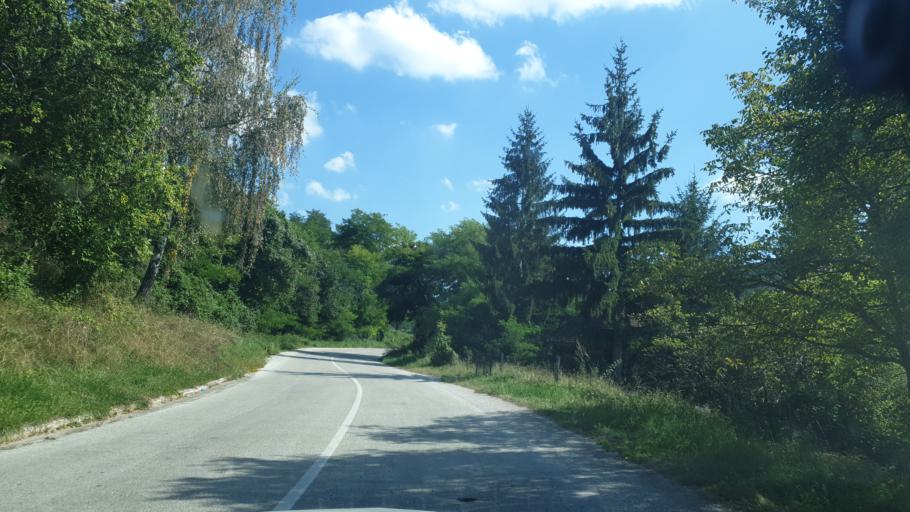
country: RS
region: Central Serbia
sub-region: Zlatiborski Okrug
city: Kosjeric
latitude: 44.0095
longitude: 20.0438
